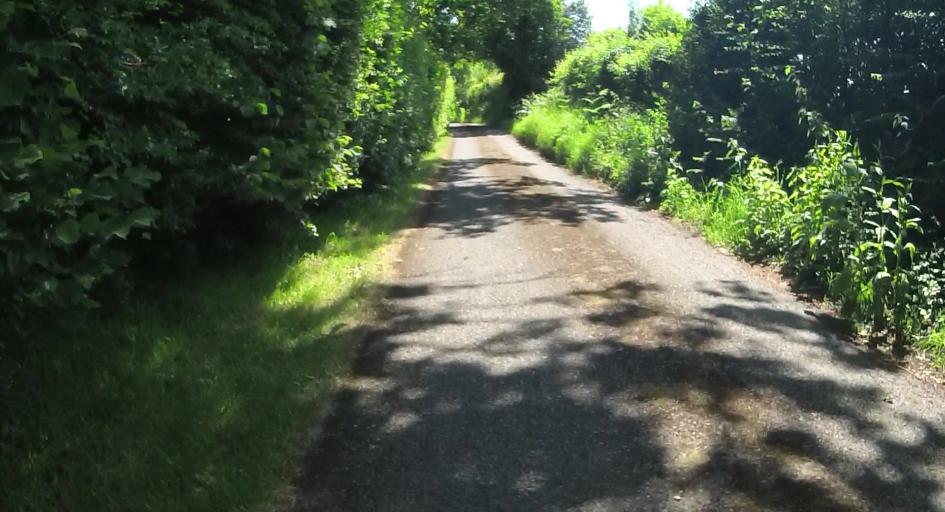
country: GB
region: England
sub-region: Hampshire
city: Kingsclere
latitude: 51.3485
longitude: -1.2747
